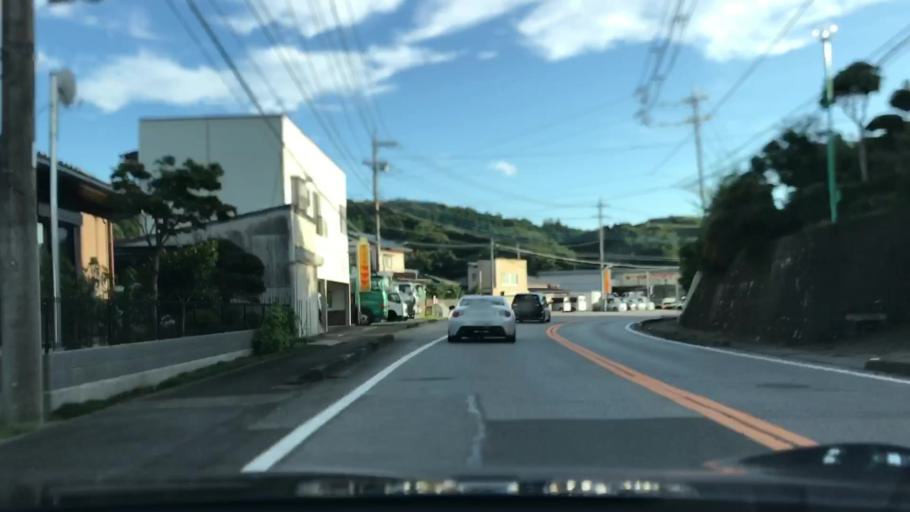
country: JP
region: Tochigi
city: Motegi
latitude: 36.5341
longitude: 140.2060
